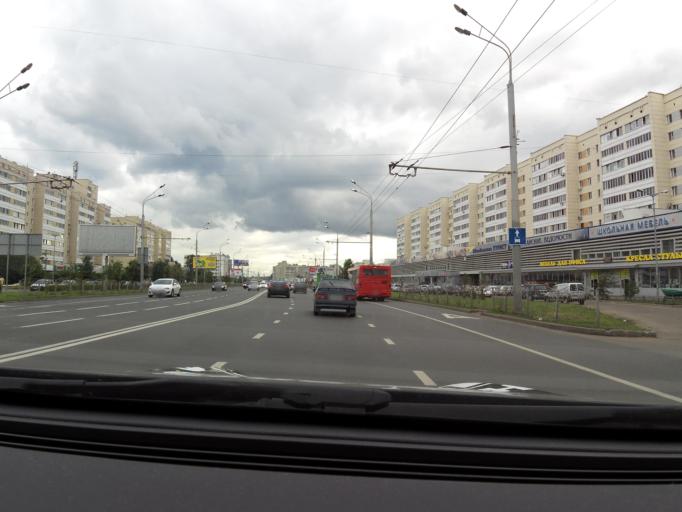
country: RU
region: Tatarstan
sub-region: Gorod Kazan'
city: Kazan
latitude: 55.8194
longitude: 49.1040
